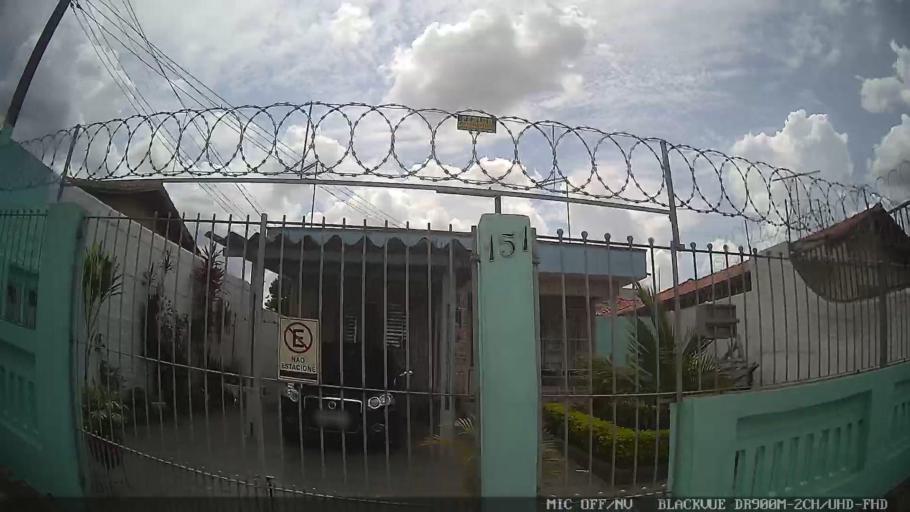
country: BR
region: Sao Paulo
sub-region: Suzano
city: Suzano
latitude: -23.5349
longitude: -46.3140
